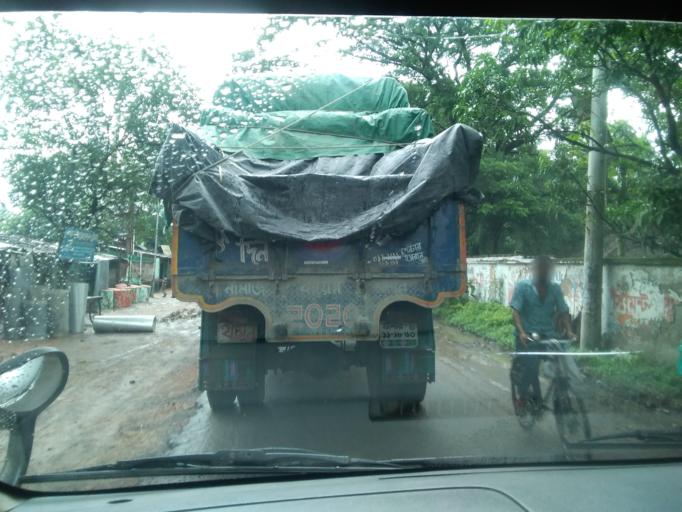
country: IN
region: West Bengal
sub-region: North 24 Parganas
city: Taki
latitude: 22.3461
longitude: 89.1042
